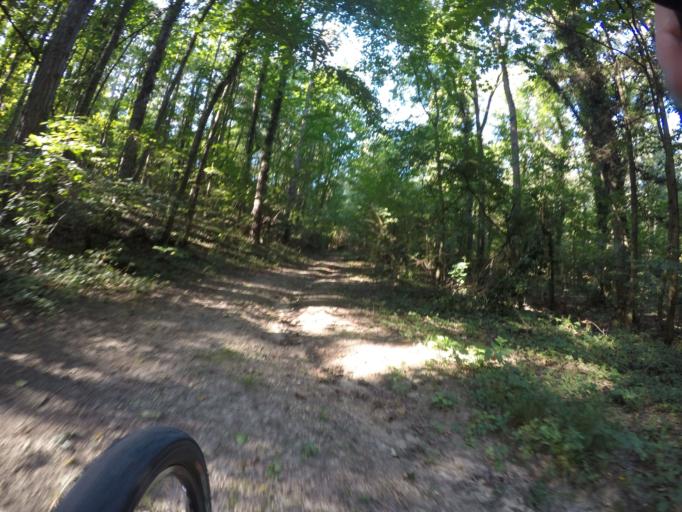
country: AT
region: Lower Austria
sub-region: Politischer Bezirk Bruck an der Leitha
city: Mannersdorf am Leithagebirge
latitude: 47.9611
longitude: 16.6136
